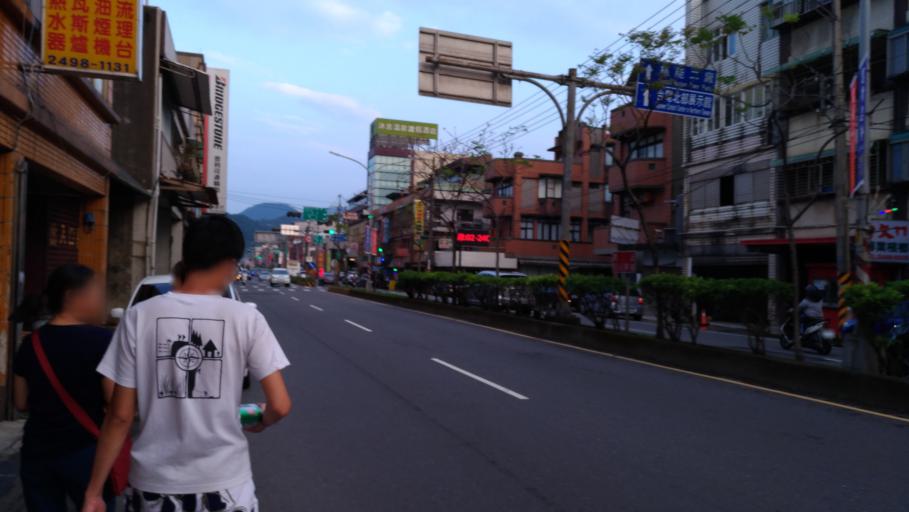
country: TW
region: Taiwan
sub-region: Keelung
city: Keelung
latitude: 25.2164
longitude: 121.6427
